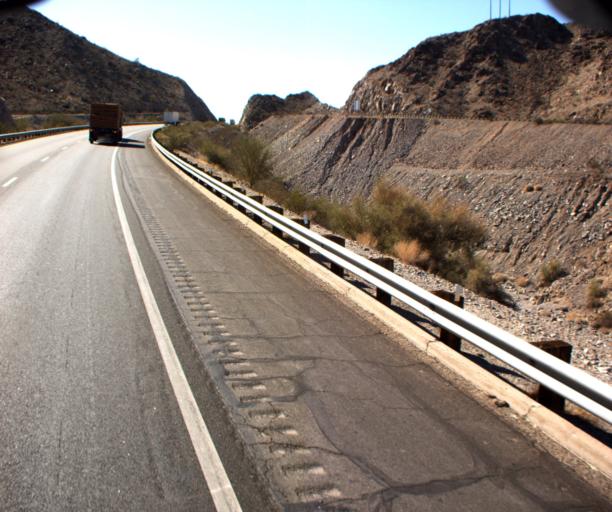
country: US
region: Arizona
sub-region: Yuma County
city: Fortuna Foothills
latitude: 32.6597
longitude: -114.3213
